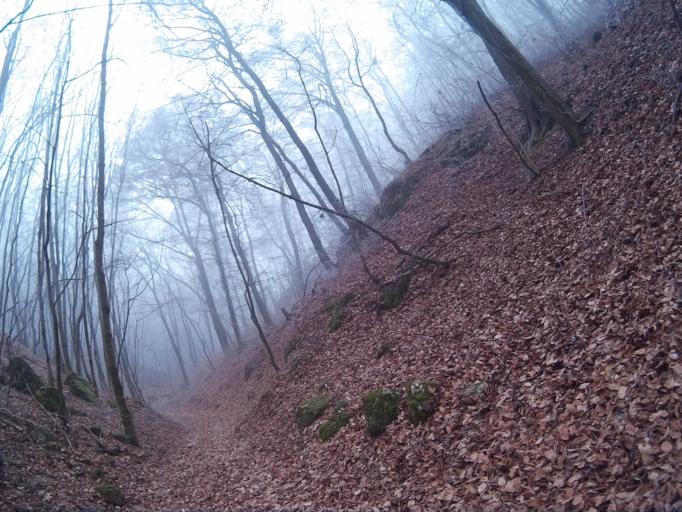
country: HU
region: Fejer
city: Bodajk
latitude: 47.3637
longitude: 18.2730
